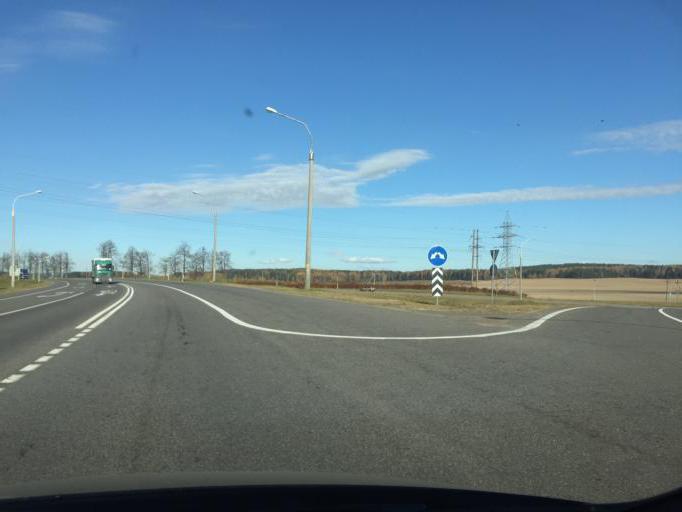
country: BY
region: Minsk
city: Slabada
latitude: 54.0193
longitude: 27.8890
